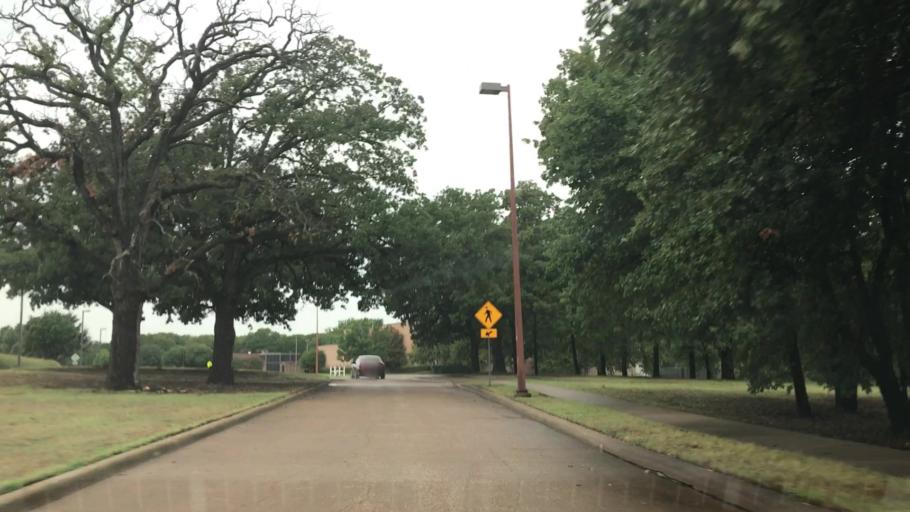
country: US
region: Texas
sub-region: Denton County
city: Highland Village
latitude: 33.0429
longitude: -97.0540
